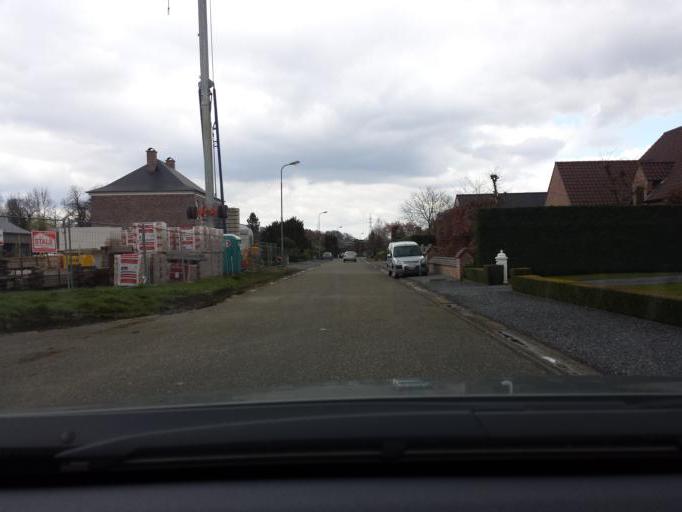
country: BE
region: Flanders
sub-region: Provincie Vlaams-Brabant
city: Diest
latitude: 50.9709
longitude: 5.0383
